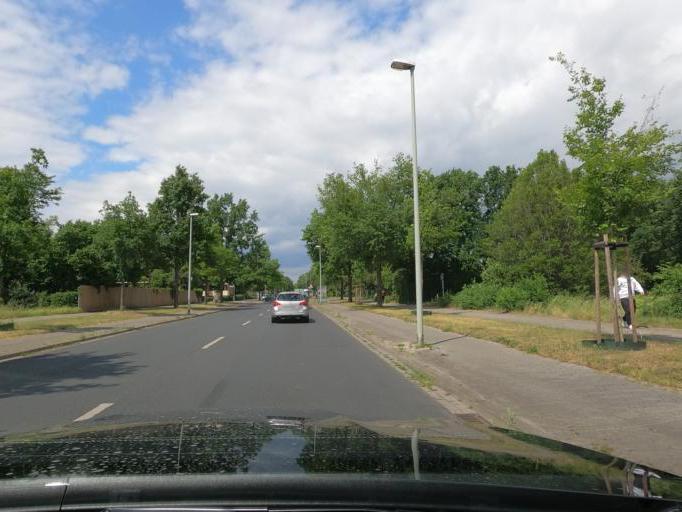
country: DE
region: Lower Saxony
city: Isernhagen Farster Bauerschaft
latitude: 52.3952
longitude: 9.8164
